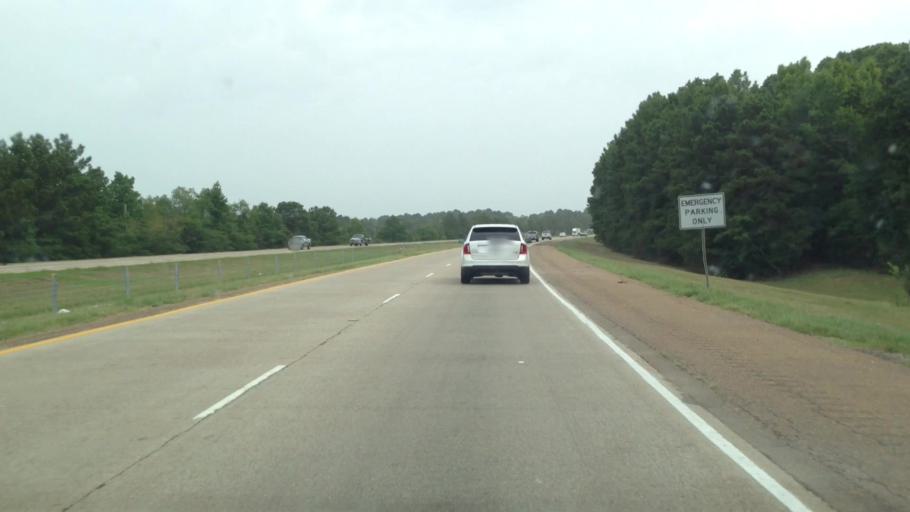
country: US
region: Louisiana
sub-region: Caddo Parish
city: Shreveport
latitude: 32.4273
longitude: -93.8385
